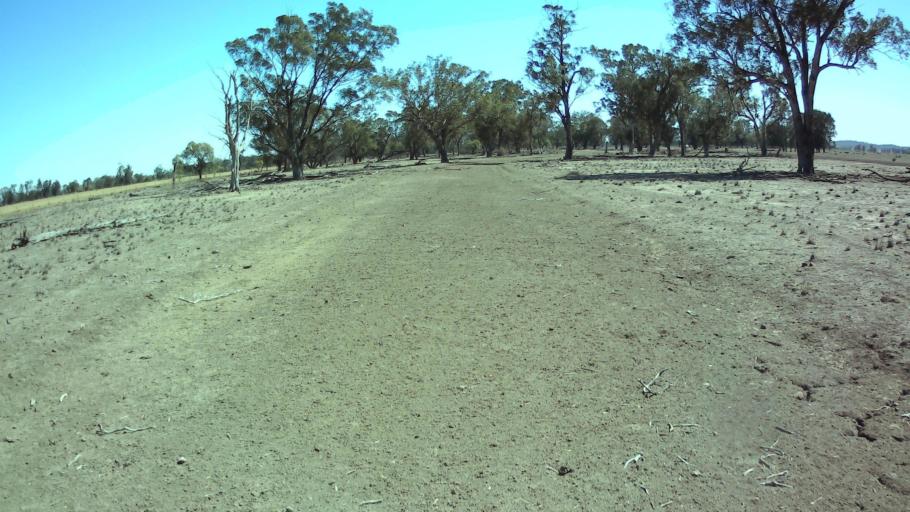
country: AU
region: New South Wales
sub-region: Bland
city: West Wyalong
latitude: -33.7665
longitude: 147.6575
